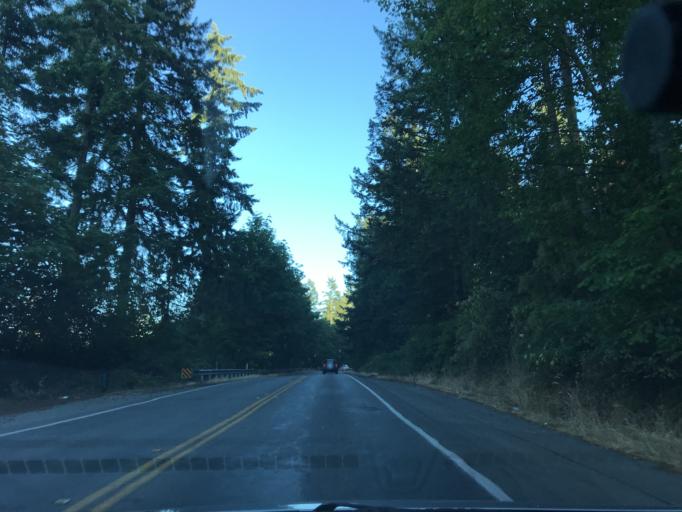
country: US
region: Washington
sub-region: King County
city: Pacific
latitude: 47.2592
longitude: -122.1884
